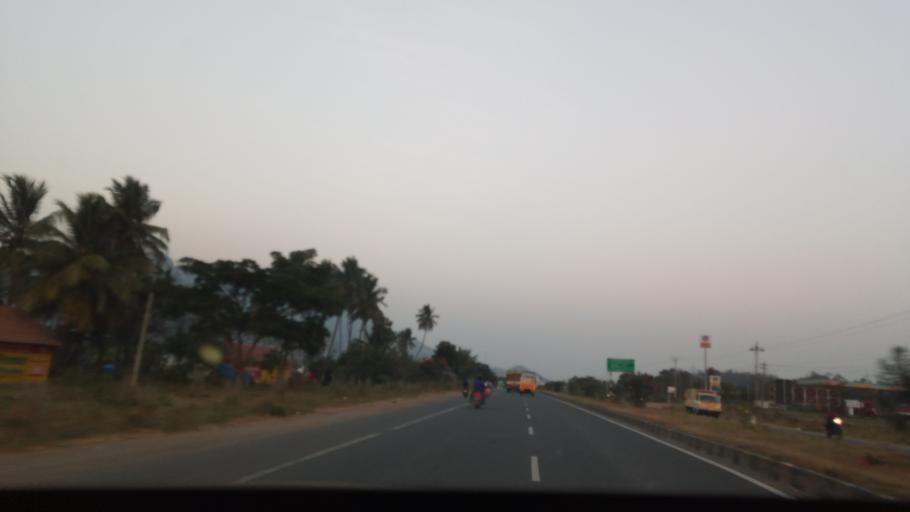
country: IN
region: Tamil Nadu
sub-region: Salem
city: Belur
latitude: 11.6652
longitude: 78.3141
